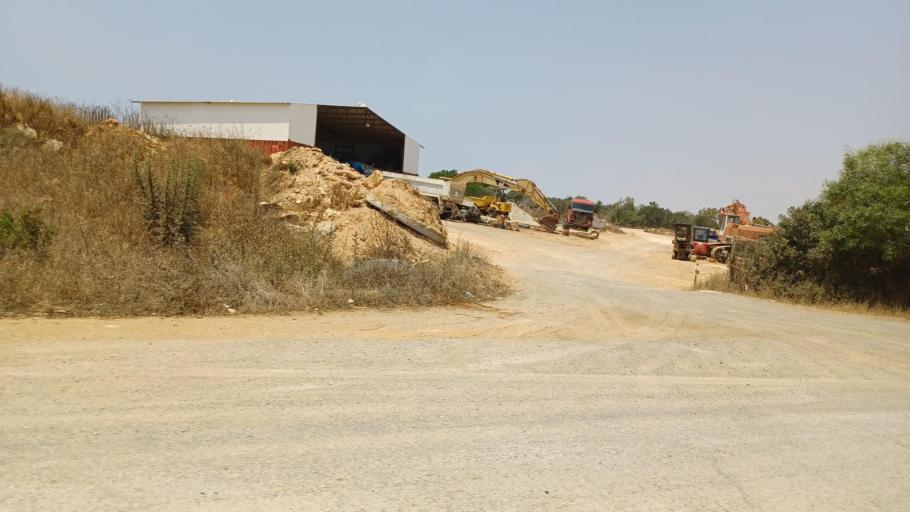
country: CY
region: Ammochostos
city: Liopetri
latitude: 34.9667
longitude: 33.8493
